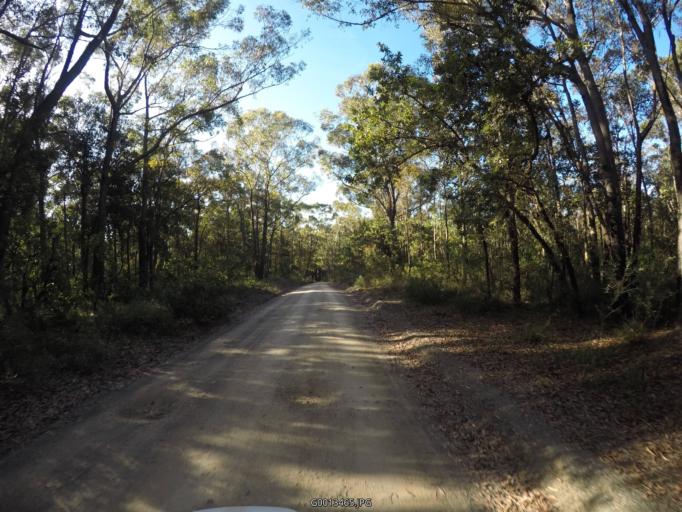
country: AU
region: New South Wales
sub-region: Lake Macquarie Shire
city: Cooranbong
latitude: -33.0684
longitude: 151.3351
